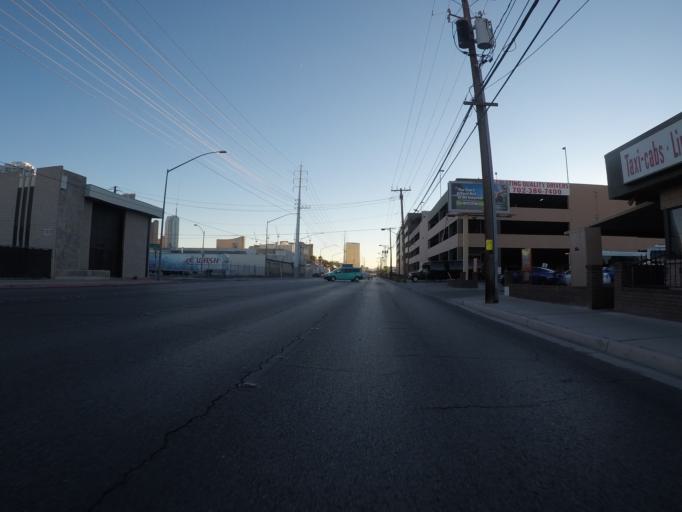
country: US
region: Nevada
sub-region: Clark County
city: Las Vegas
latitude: 36.1490
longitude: -115.1616
